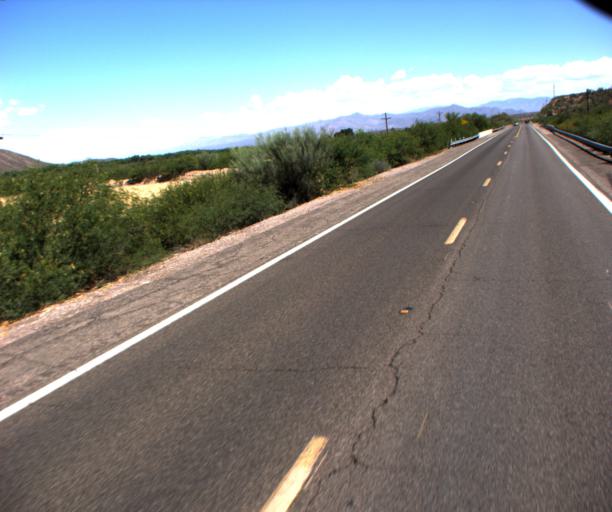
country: US
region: Arizona
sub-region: Pinal County
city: Mammoth
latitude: 32.8990
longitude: -110.7171
